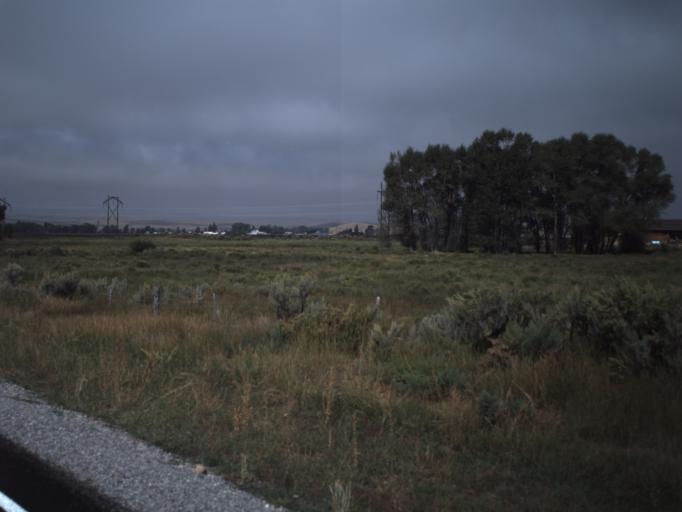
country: US
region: Utah
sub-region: Rich County
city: Randolph
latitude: 41.5174
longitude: -111.1429
